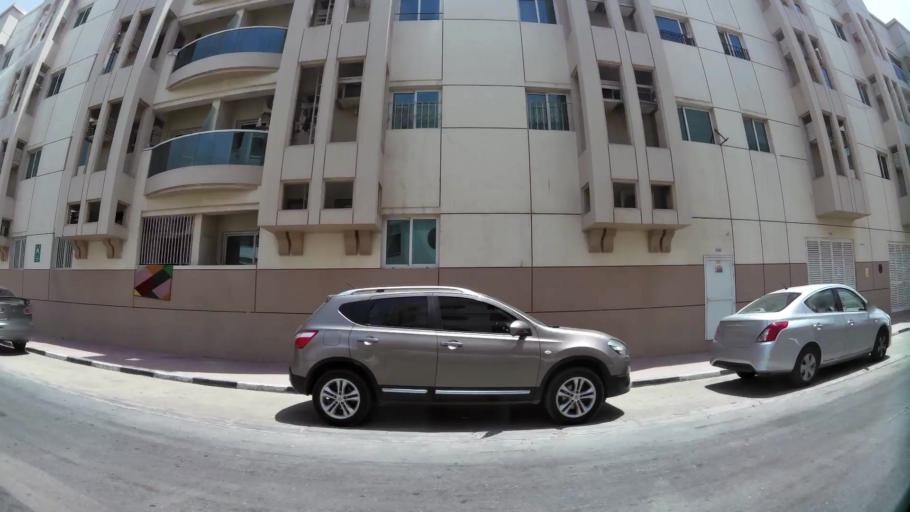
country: AE
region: Ash Shariqah
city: Sharjah
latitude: 25.2769
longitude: 55.4103
